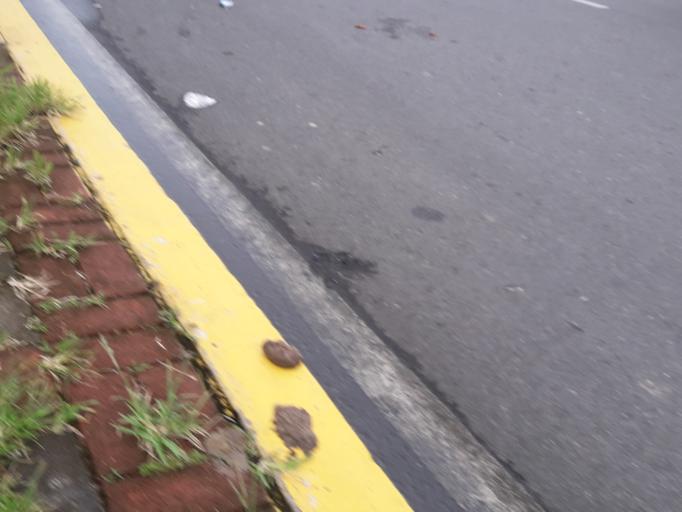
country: EC
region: Napo
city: Tena
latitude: -1.0014
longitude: -77.8137
